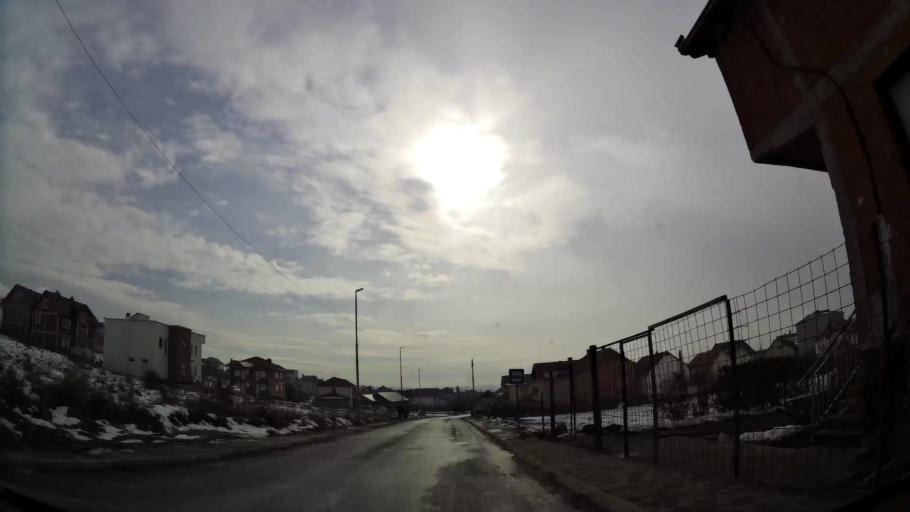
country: XK
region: Pristina
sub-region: Komuna e Prishtines
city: Pristina
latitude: 42.6886
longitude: 21.1658
